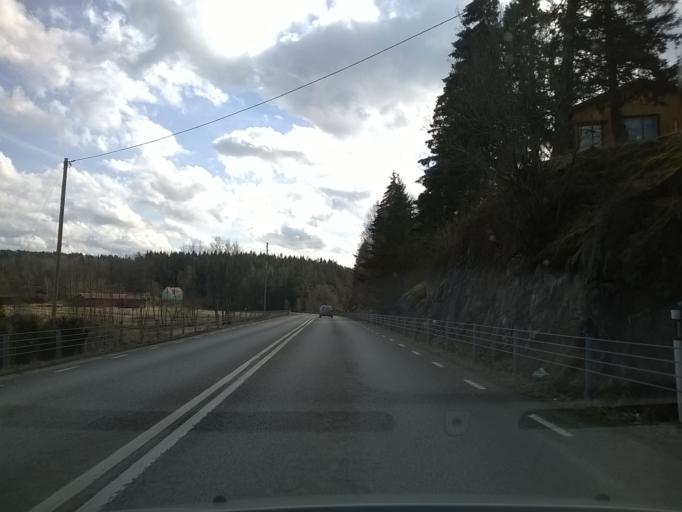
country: SE
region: Vaestra Goetaland
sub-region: Orust
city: Henan
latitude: 58.1899
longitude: 11.6901
